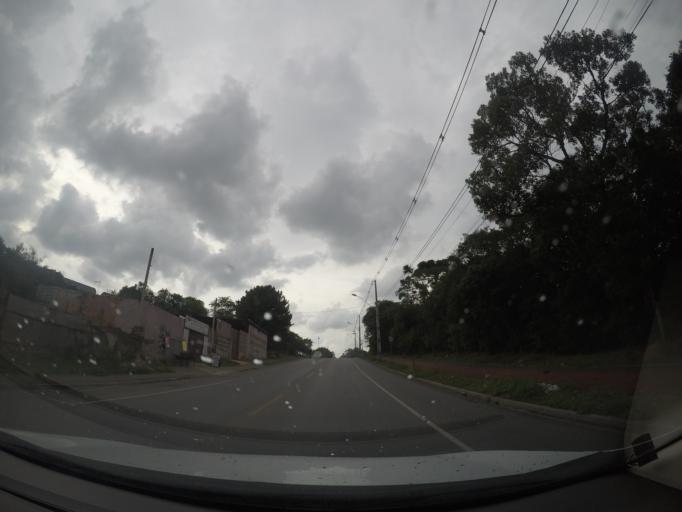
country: BR
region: Parana
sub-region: Sao Jose Dos Pinhais
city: Sao Jose dos Pinhais
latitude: -25.5470
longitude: -49.2445
